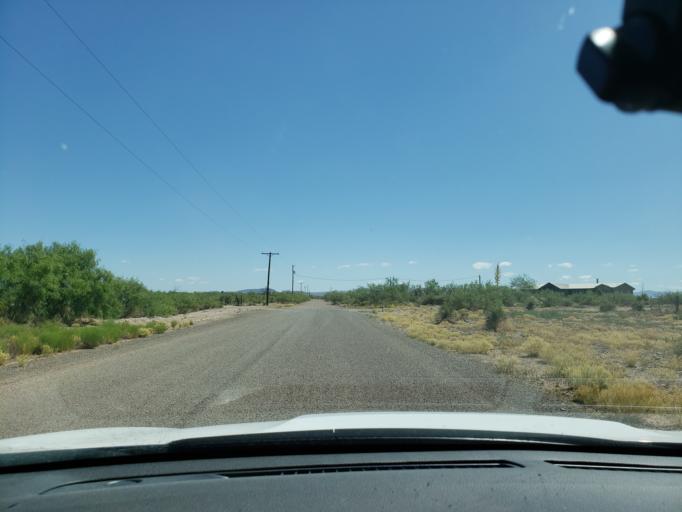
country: US
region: Texas
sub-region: Presidio County
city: Marfa
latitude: 30.5917
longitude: -104.4919
